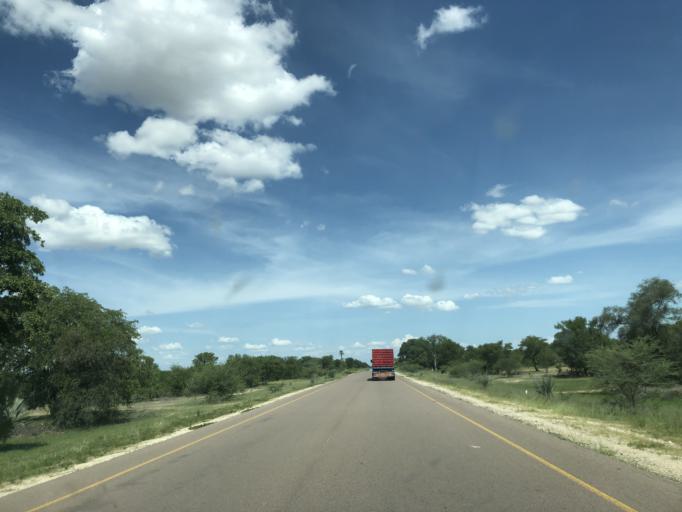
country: AO
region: Cunene
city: Ondjiva
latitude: -16.8931
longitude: 15.4991
